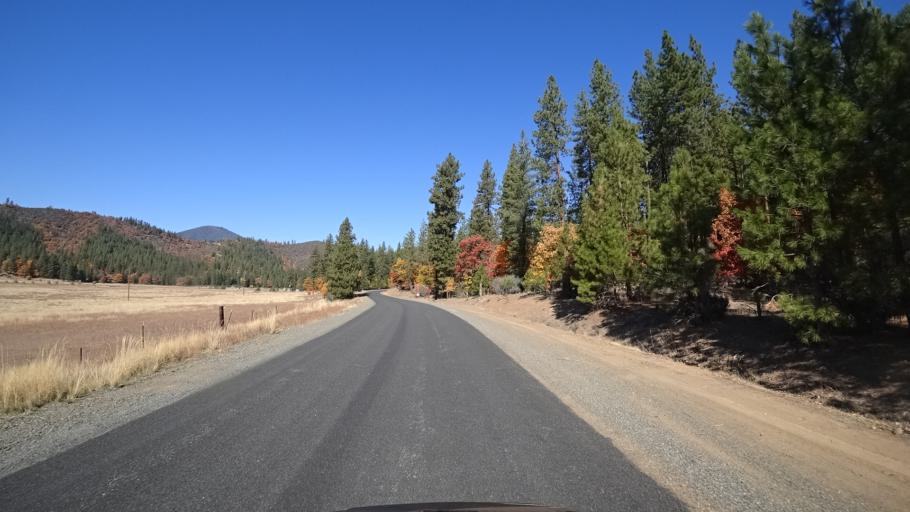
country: US
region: California
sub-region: Siskiyou County
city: Yreka
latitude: 41.6367
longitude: -122.8731
